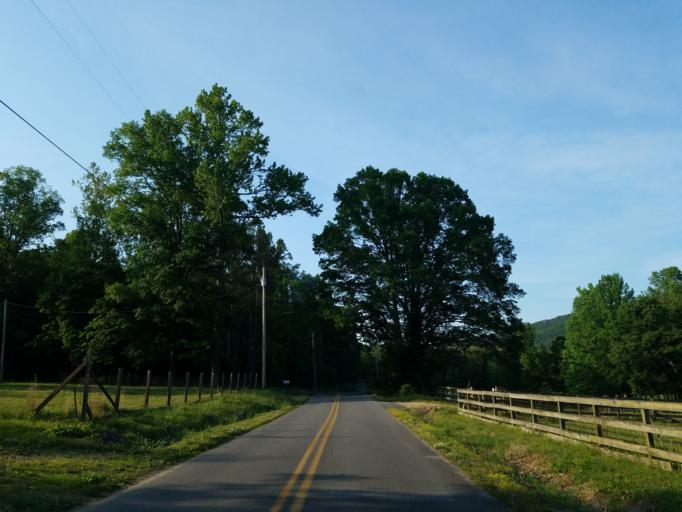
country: US
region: Georgia
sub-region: Gordon County
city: Calhoun
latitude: 34.5536
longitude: -85.1056
